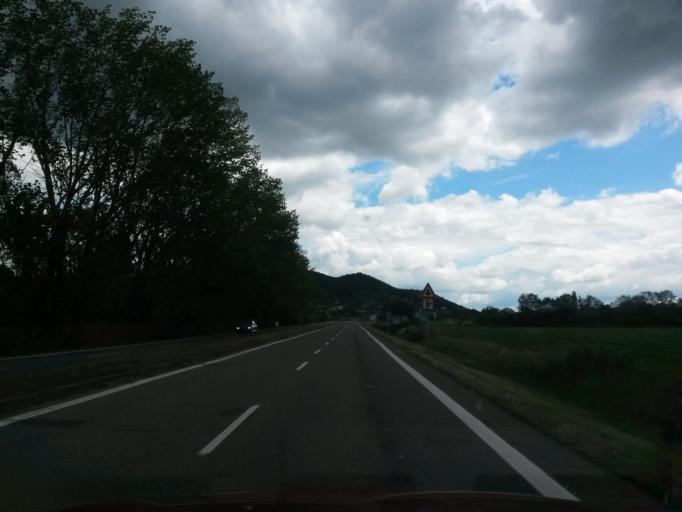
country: SK
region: Kosicky
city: Vinne
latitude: 48.7986
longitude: 21.9630
